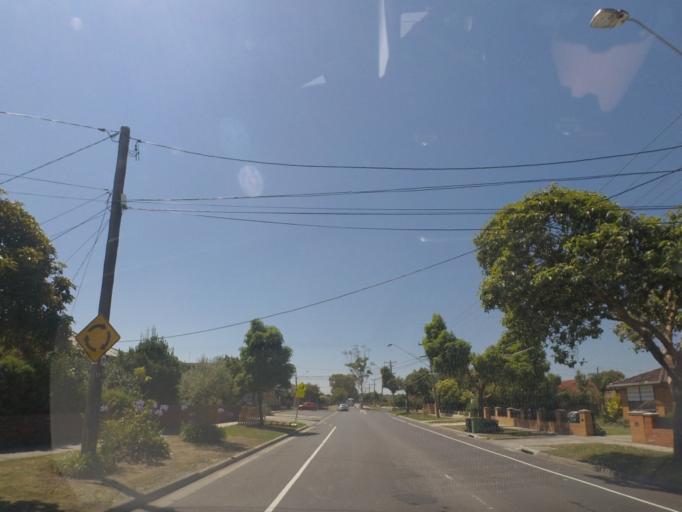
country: AU
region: Victoria
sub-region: Darebin
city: Reservoir
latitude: -37.7054
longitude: 144.9900
